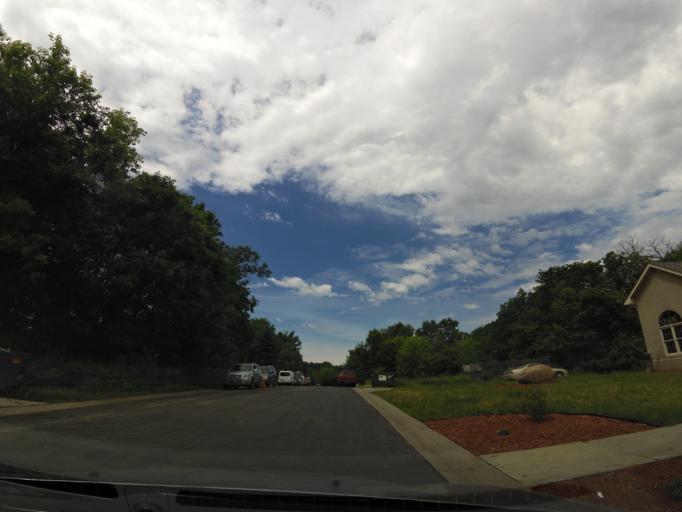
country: US
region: Minnesota
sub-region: Scott County
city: Prior Lake
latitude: 44.7554
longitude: -93.4519
